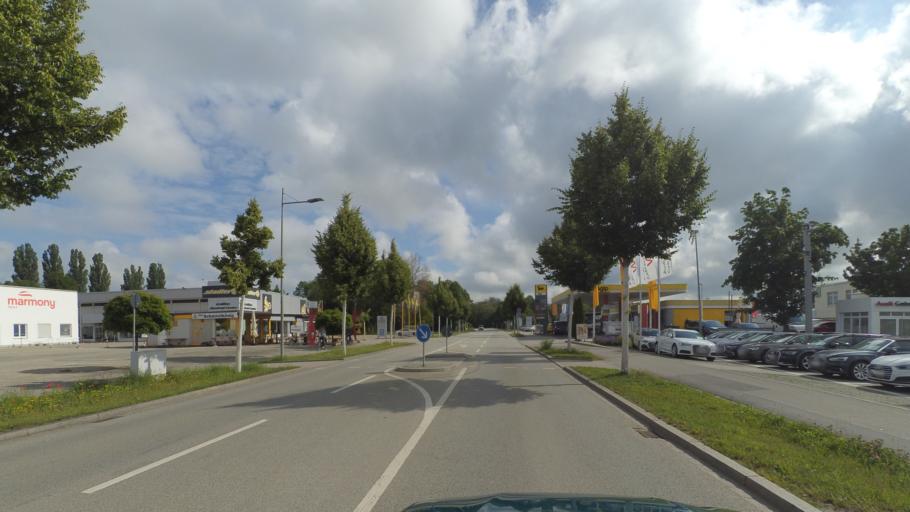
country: DE
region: Bavaria
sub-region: Lower Bavaria
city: Straubing
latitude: 48.8902
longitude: 12.5767
